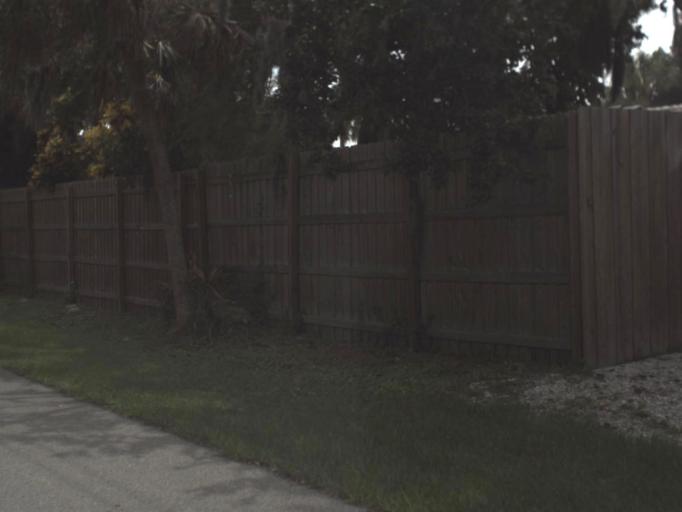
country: US
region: Florida
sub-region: Sarasota County
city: South Sarasota
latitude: 27.2811
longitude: -82.5523
